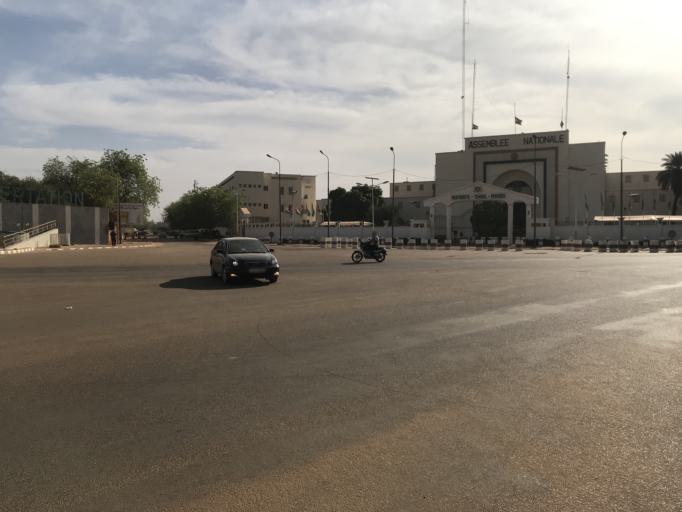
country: NE
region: Niamey
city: Niamey
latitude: 13.5116
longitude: 2.1136
